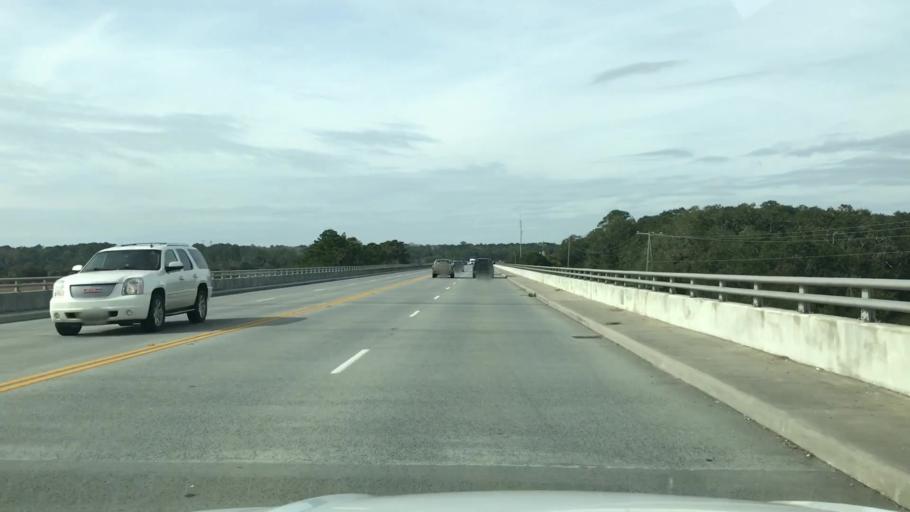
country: US
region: South Carolina
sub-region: Charleston County
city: Charleston
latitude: 32.7522
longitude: -80.0161
